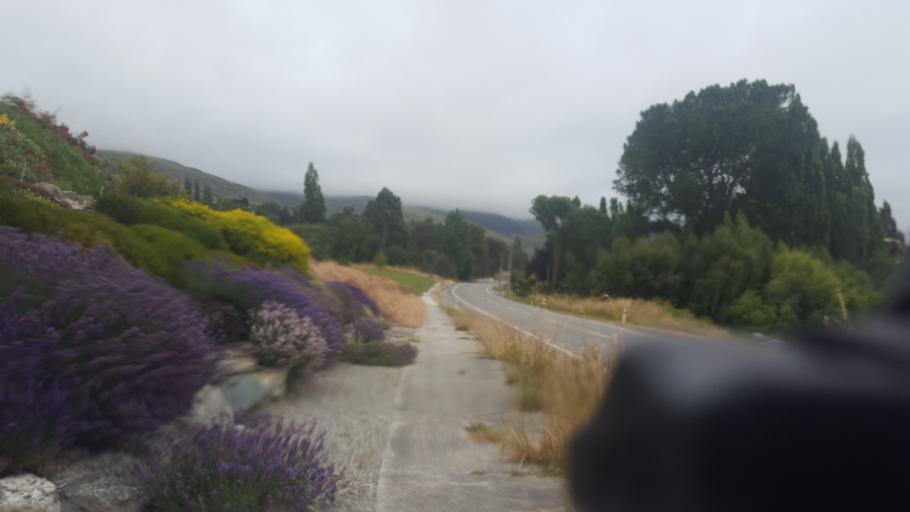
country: NZ
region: Otago
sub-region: Queenstown-Lakes District
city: Kingston
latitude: -45.5338
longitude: 169.3010
